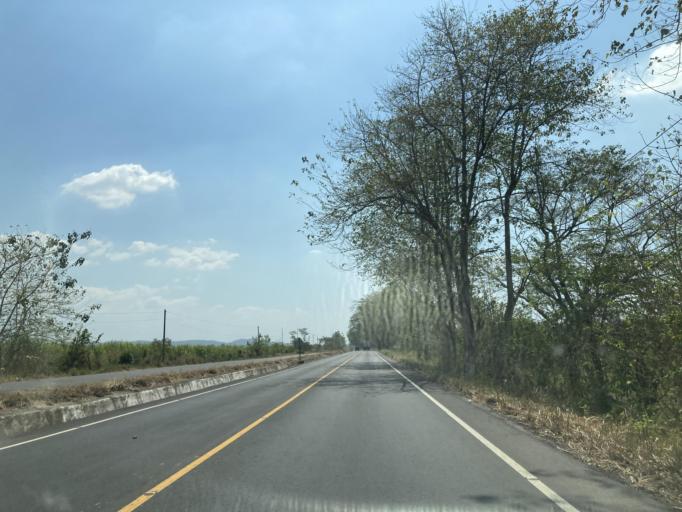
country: GT
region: Escuintla
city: Guanagazapa
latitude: 14.2034
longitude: -90.7049
